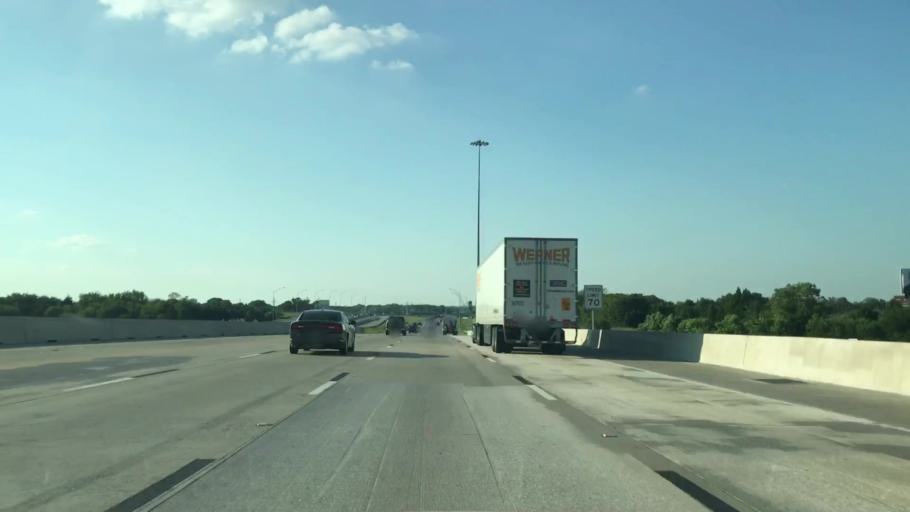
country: US
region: Texas
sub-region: Denton County
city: Highland Village
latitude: 33.0723
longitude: -97.0199
